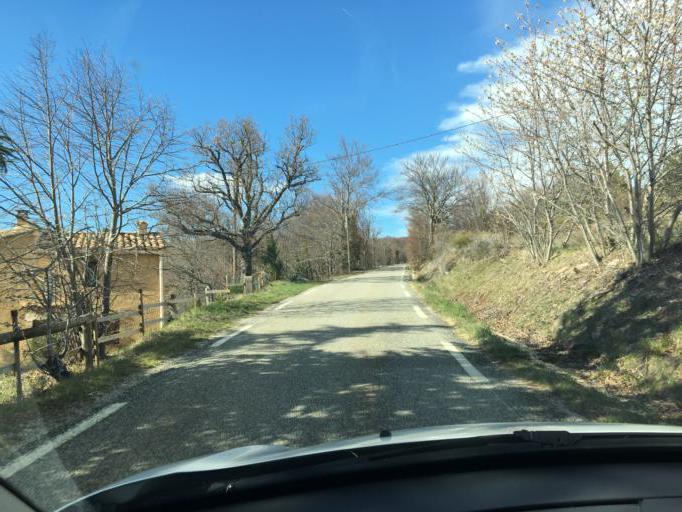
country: FR
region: Provence-Alpes-Cote d'Azur
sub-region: Departement du Vaucluse
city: Saint-Saturnin-les-Apt
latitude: 43.9722
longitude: 5.4616
